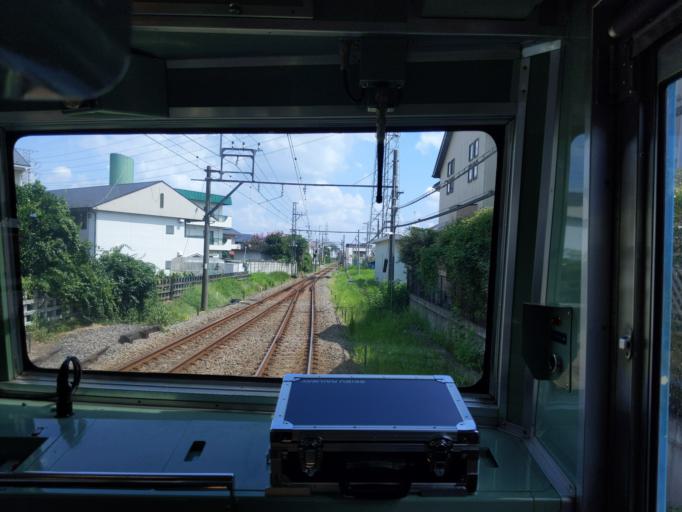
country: JP
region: Tokyo
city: Kamirenjaku
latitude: 35.6967
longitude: 139.5280
